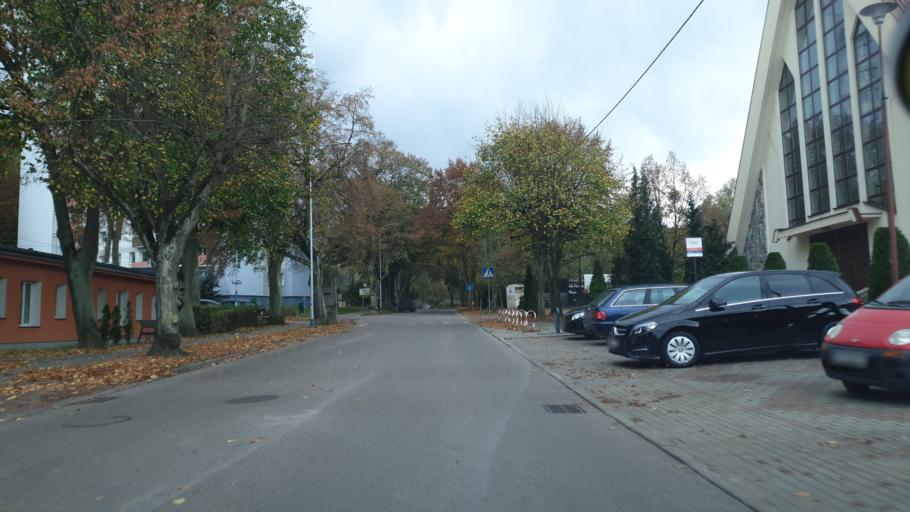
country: PL
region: Pomeranian Voivodeship
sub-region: Sopot
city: Sopot
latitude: 54.3899
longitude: 18.5689
